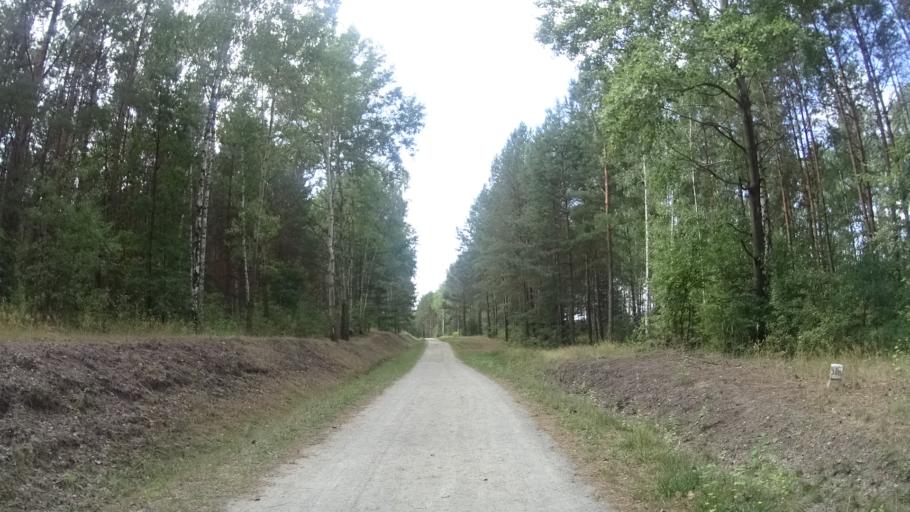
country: PL
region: Lubusz
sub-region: Powiat zarski
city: Leknica
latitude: 51.5371
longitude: 14.7756
